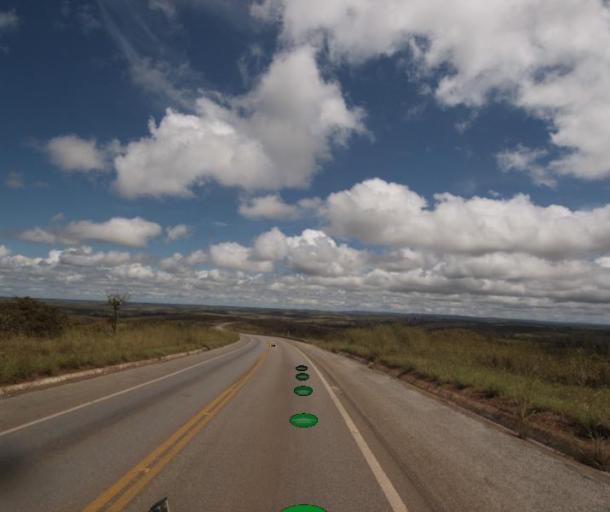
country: BR
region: Federal District
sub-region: Brasilia
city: Brasilia
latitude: -15.7566
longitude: -48.4352
